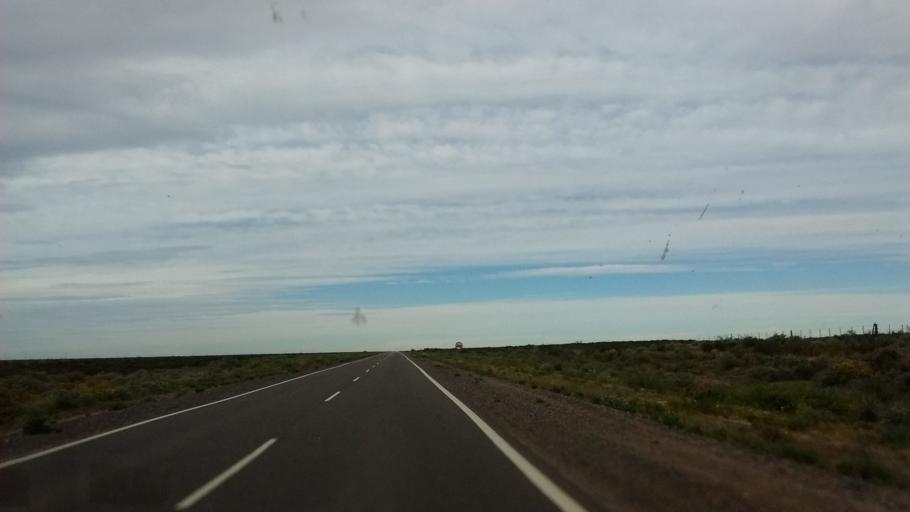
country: AR
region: Rio Negro
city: Contraalmirante Cordero
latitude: -38.4699
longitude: -68.0497
